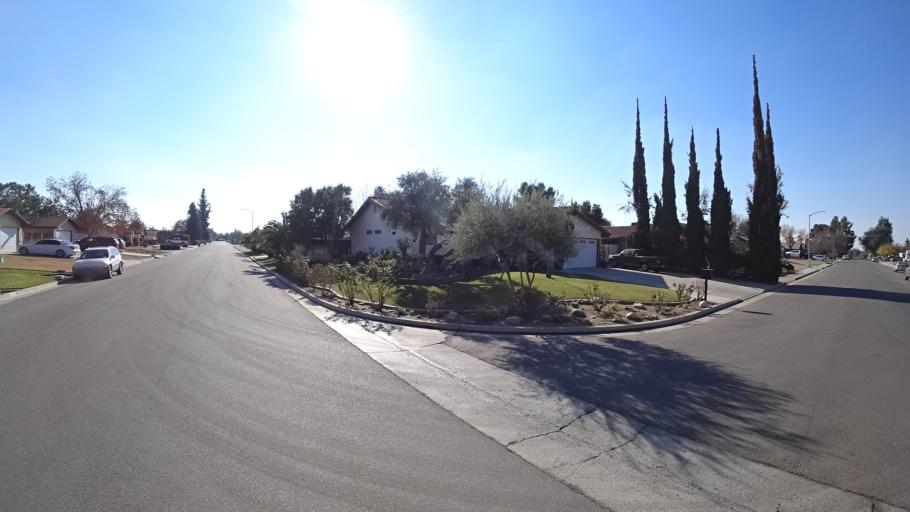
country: US
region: California
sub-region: Kern County
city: Greenfield
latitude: 35.3061
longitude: -119.0429
